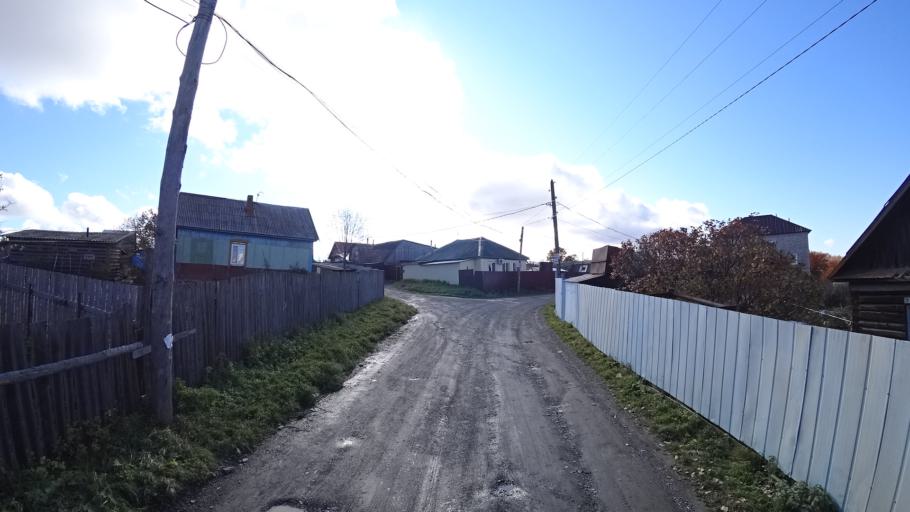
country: RU
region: Khabarovsk Krai
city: Amursk
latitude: 50.2342
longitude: 136.9193
